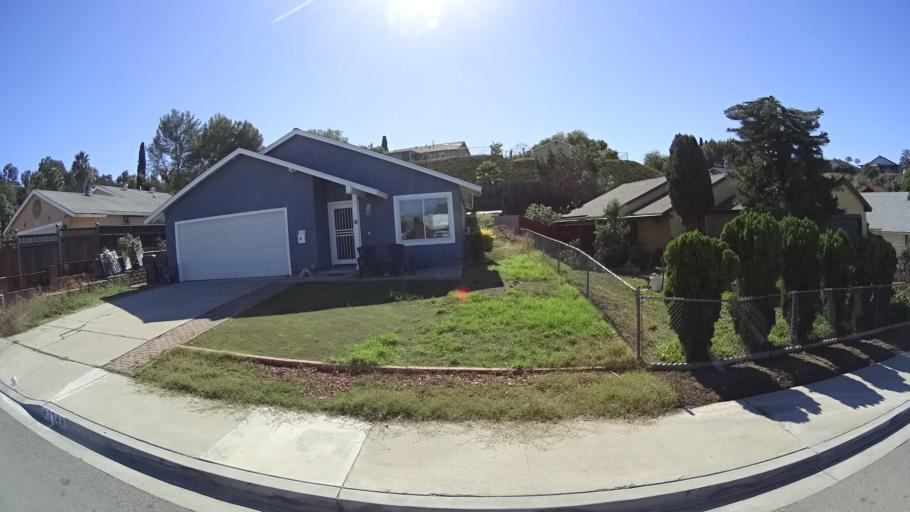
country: US
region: California
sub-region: San Diego County
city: La Presa
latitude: 32.6997
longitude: -117.0174
